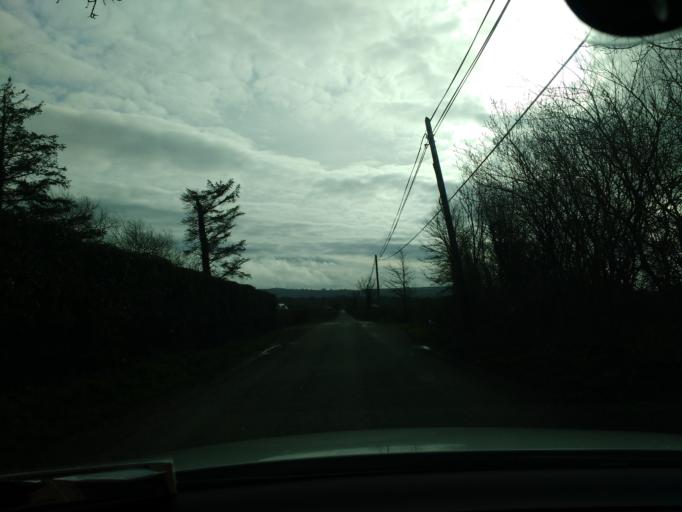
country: IE
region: Leinster
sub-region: Laois
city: Rathdowney
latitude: 52.6741
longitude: -7.5944
